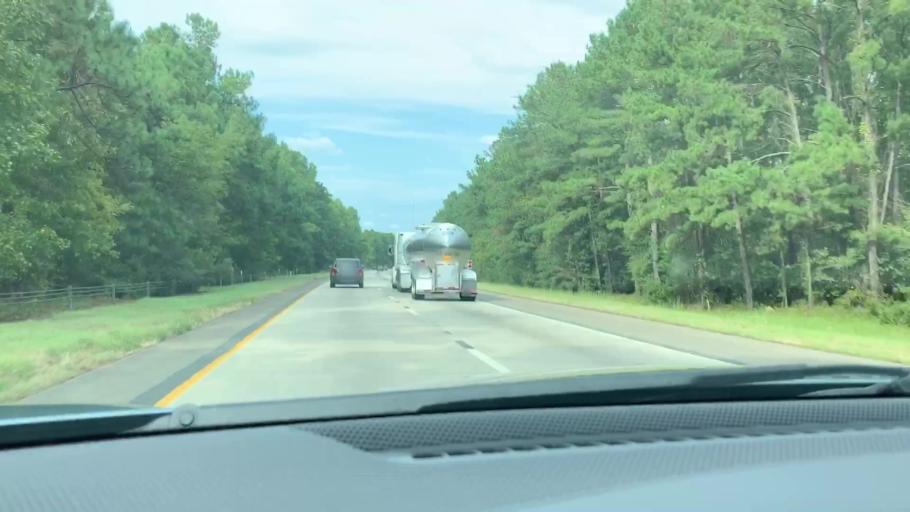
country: US
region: South Carolina
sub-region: Colleton County
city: Walterboro
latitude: 32.8863
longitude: -80.7142
